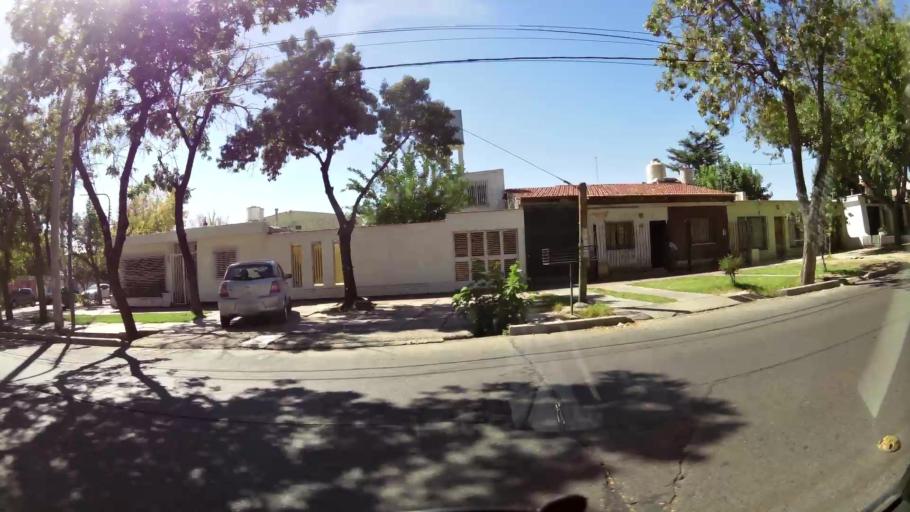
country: AR
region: Mendoza
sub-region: Departamento de Godoy Cruz
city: Godoy Cruz
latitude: -32.9177
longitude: -68.8594
